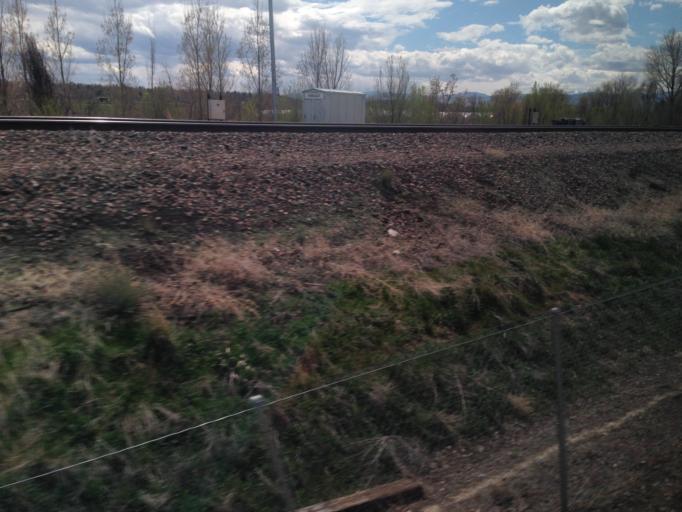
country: US
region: Colorado
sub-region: Adams County
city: Berkley
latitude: 39.8043
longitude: -105.0310
